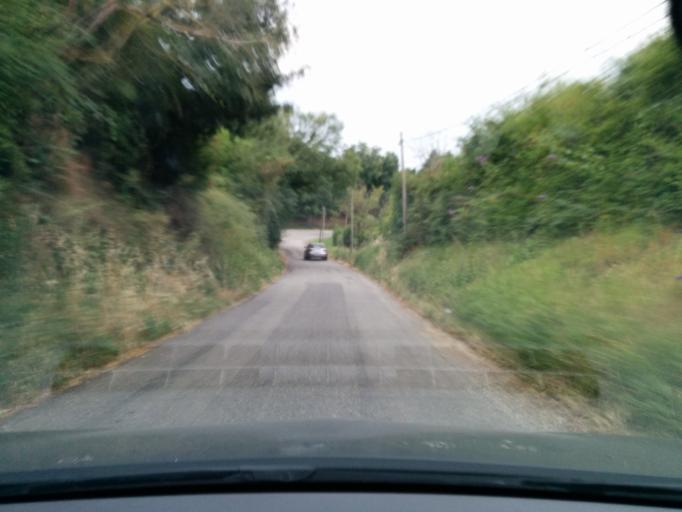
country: FR
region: Midi-Pyrenees
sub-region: Departement de la Haute-Garonne
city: Castanet-Tolosan
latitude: 43.4908
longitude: 1.4750
